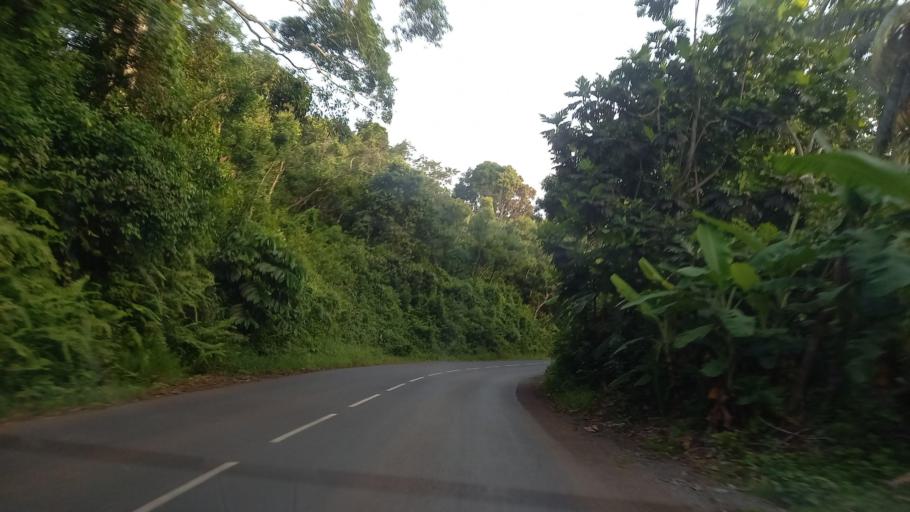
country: YT
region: Bandraboua
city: Bandraboua
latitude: -12.7346
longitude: 45.1187
